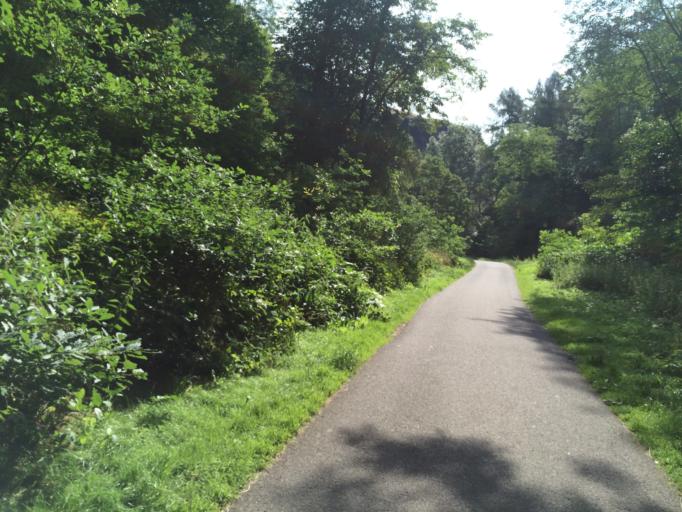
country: CZ
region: Central Bohemia
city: Horomerice
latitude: 50.0955
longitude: 14.3170
